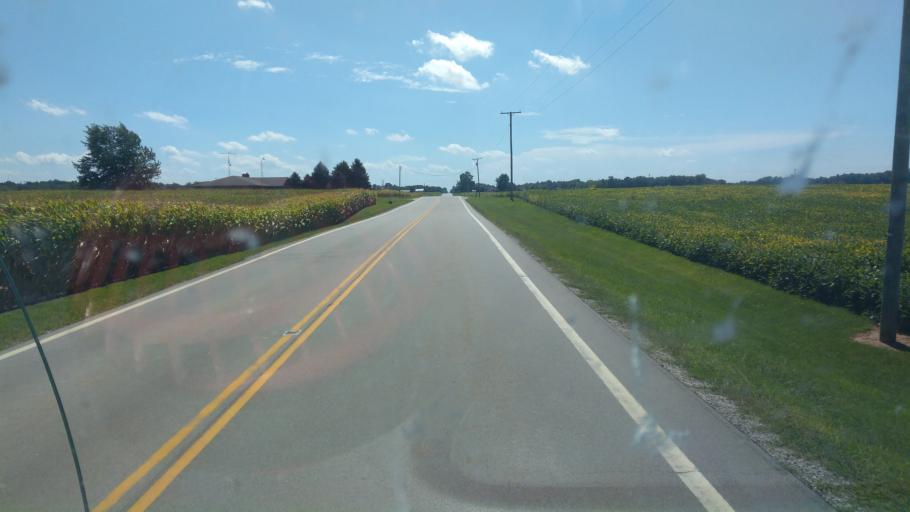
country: US
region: Ohio
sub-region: Wyandot County
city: Upper Sandusky
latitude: 40.7926
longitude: -83.1308
